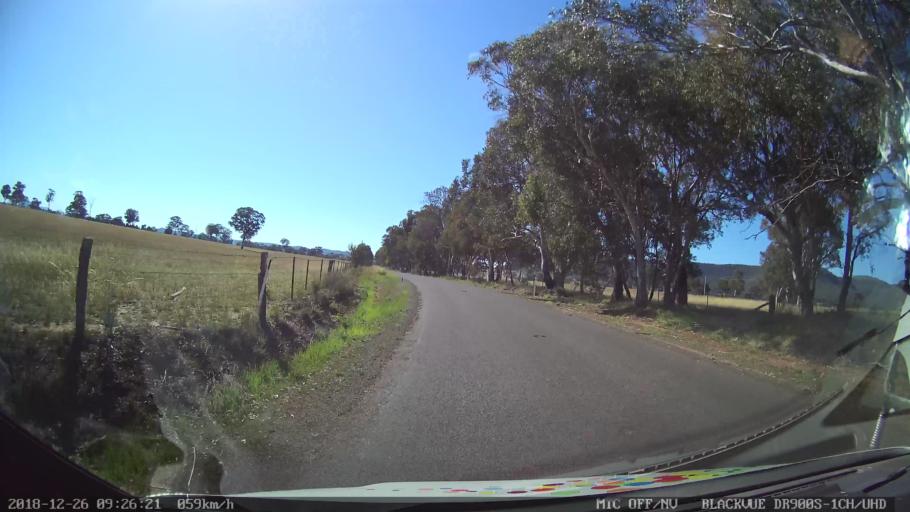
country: AU
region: New South Wales
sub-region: Mid-Western Regional
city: Kandos
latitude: -32.8279
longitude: 150.0075
